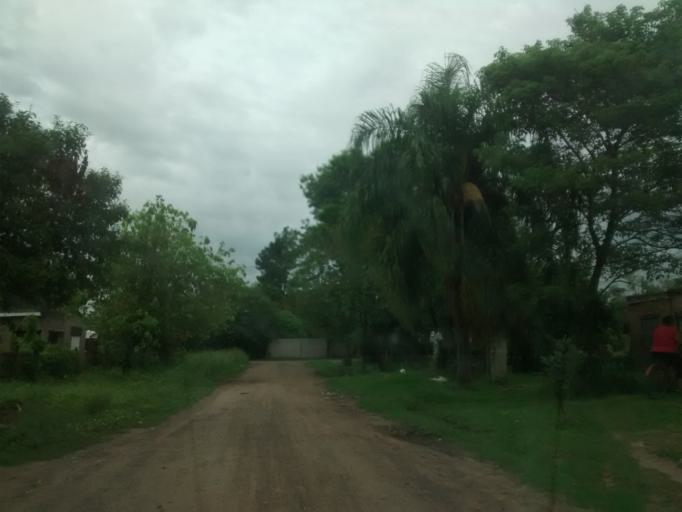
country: AR
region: Chaco
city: Puerto Tirol
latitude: -27.3766
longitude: -59.0977
